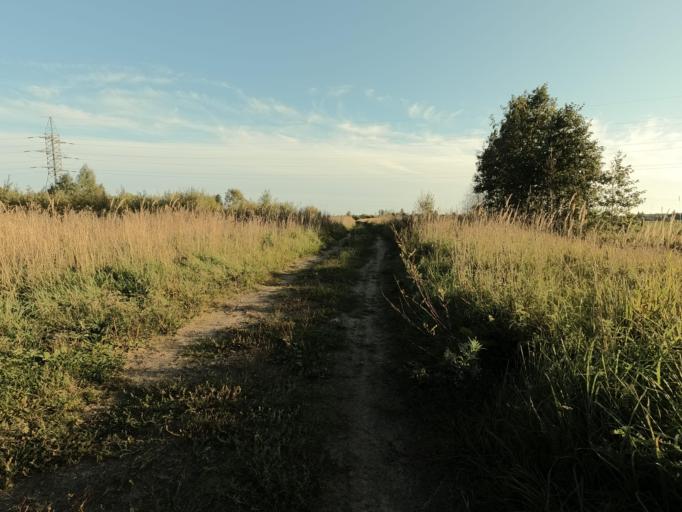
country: RU
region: Leningrad
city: Nikol'skoye
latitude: 59.7005
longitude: 30.7456
